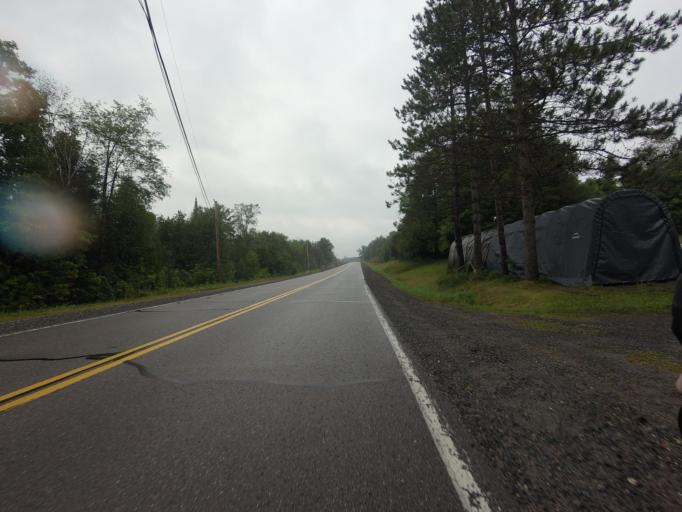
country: CA
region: Ontario
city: Perth
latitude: 45.0874
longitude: -76.4249
